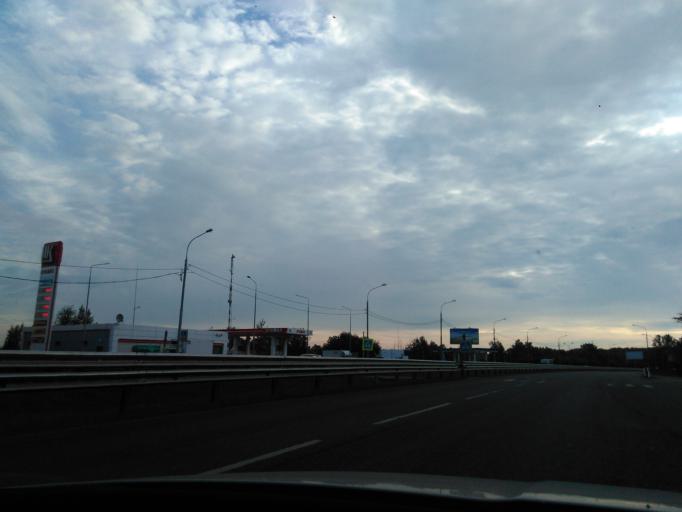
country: RU
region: Moskovskaya
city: Novopodrezkovo
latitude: 55.9772
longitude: 37.3866
